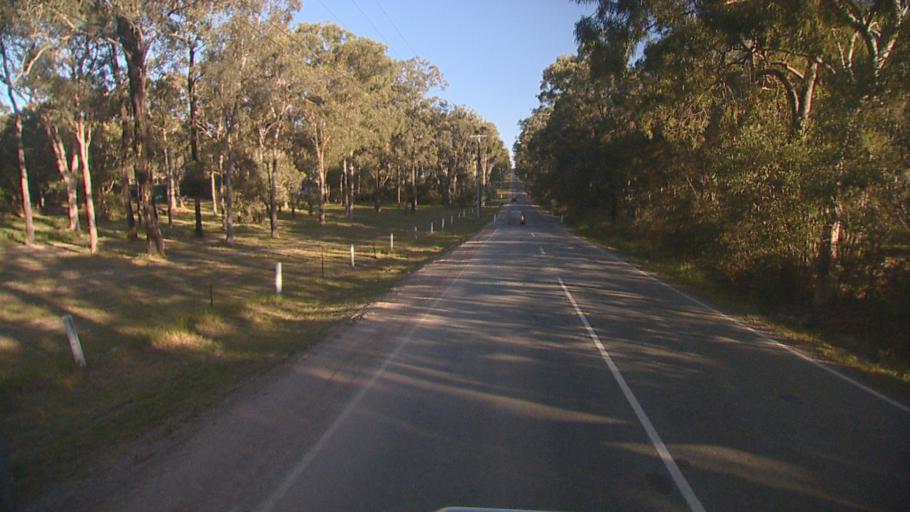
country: AU
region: Queensland
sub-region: Logan
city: Chambers Flat
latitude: -27.7710
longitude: 153.1374
